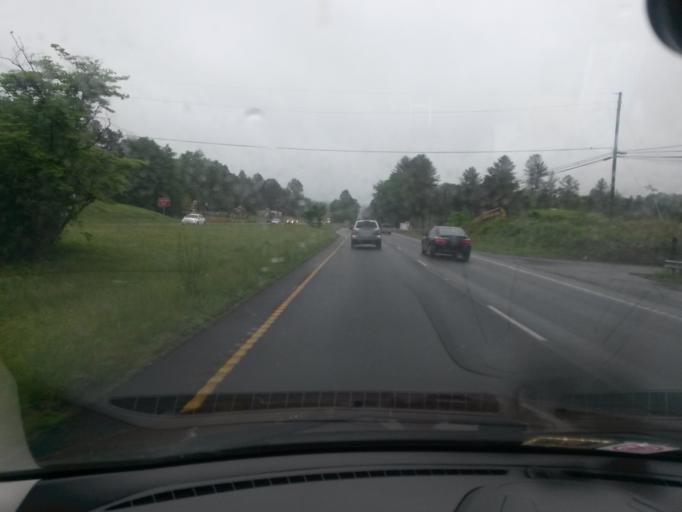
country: US
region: Virginia
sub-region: Albemarle County
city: Hollymead
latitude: 38.1423
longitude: -78.4283
